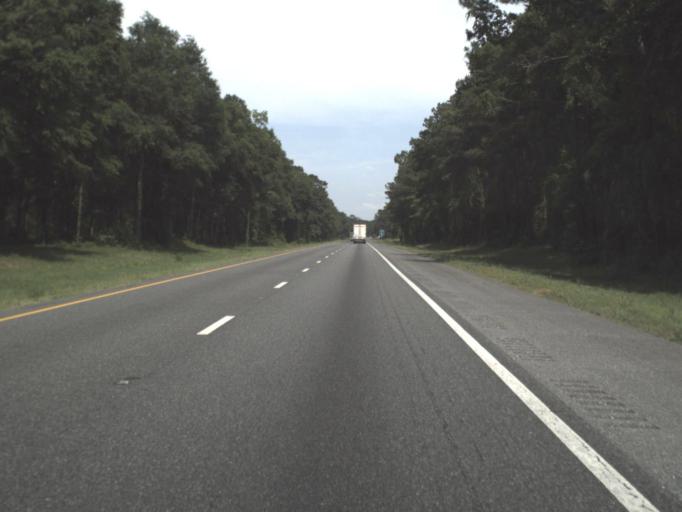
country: US
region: Florida
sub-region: Suwannee County
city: Wellborn
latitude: 30.2859
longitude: -82.8422
